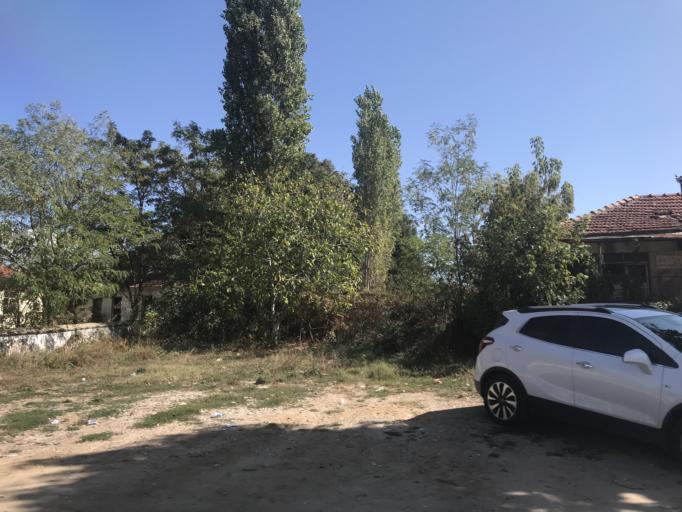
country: TR
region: Kirklareli
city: Kirklareli
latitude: 41.7749
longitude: 27.2267
